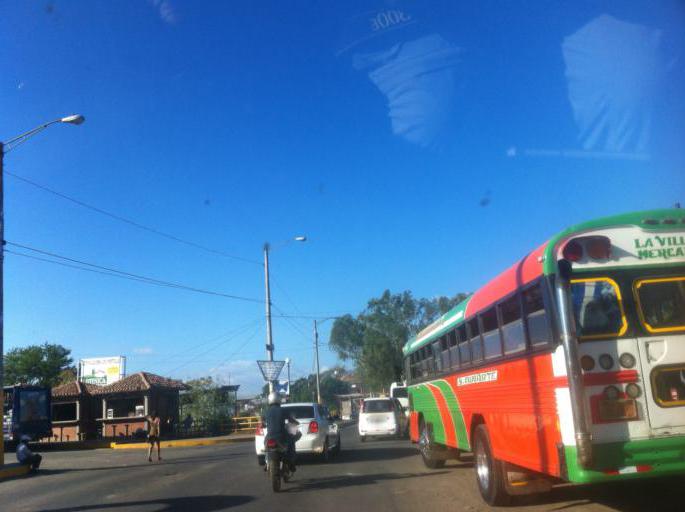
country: NI
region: Granada
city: Granada
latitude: 11.9238
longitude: -85.9642
